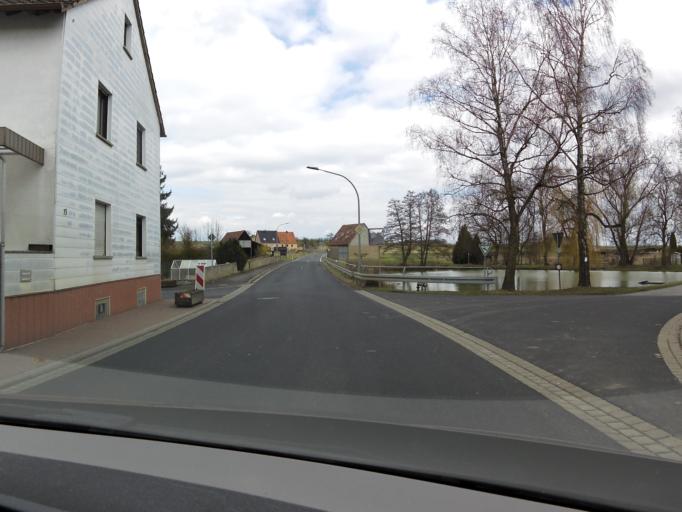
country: DE
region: Bavaria
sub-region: Regierungsbezirk Unterfranken
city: Arnstein
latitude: 49.9292
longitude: 9.9709
